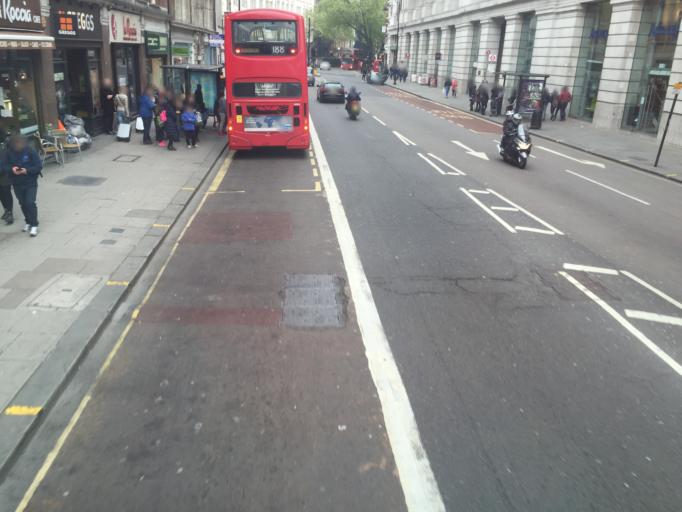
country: GB
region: England
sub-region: Greater London
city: London
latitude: 51.5198
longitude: -0.1220
